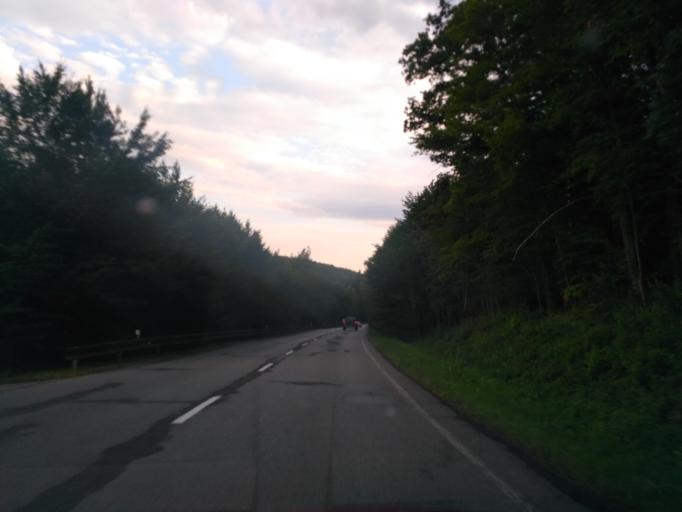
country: SK
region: Presovsky
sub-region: Okres Presov
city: Presov
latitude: 48.9687
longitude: 21.1690
